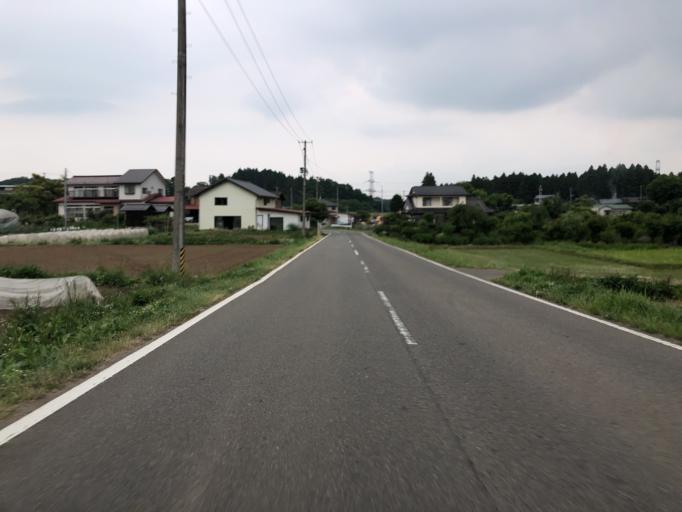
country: JP
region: Fukushima
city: Nihommatsu
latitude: 37.6417
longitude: 140.4786
